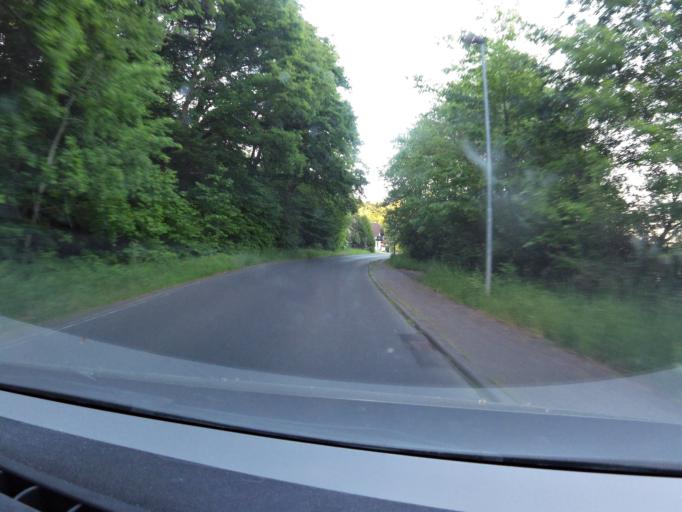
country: DE
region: Thuringia
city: Dorndorf
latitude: 50.8407
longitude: 10.0608
